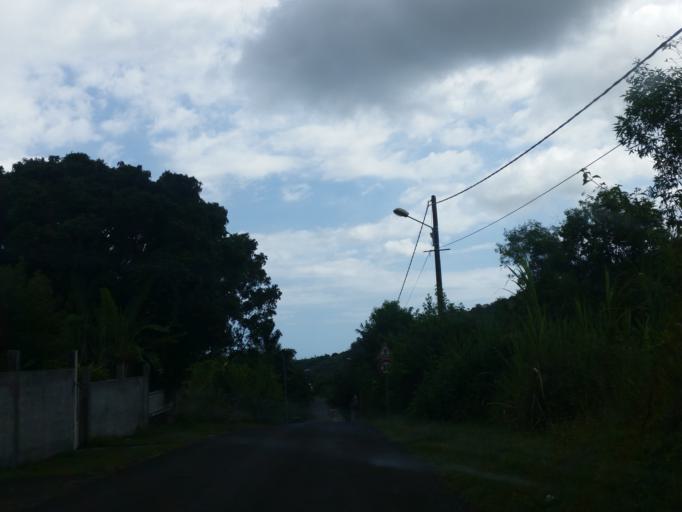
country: RE
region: Reunion
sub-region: Reunion
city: L'Entre-Deux
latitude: -21.2422
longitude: 55.4686
